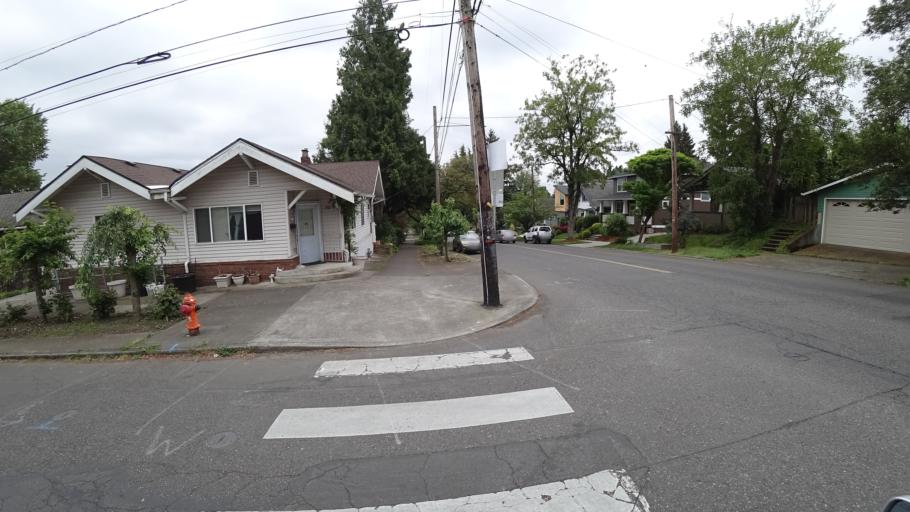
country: US
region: Oregon
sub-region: Multnomah County
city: Lents
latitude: 45.5388
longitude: -122.6045
